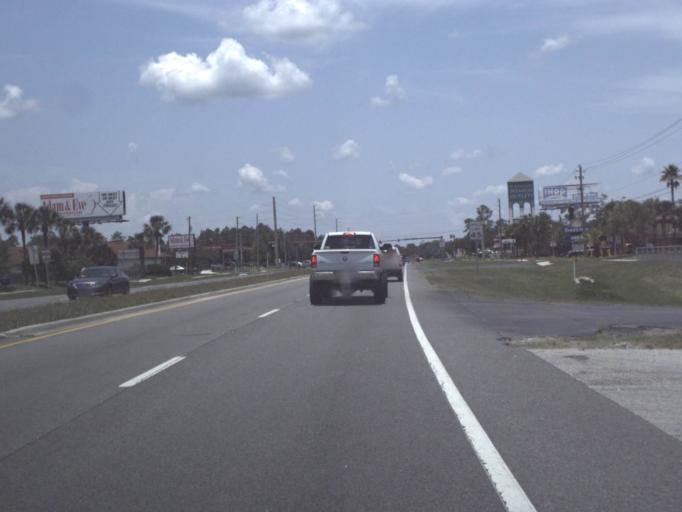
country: US
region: Florida
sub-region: Saint Johns County
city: Saint Augustine
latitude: 29.9189
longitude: -81.4147
